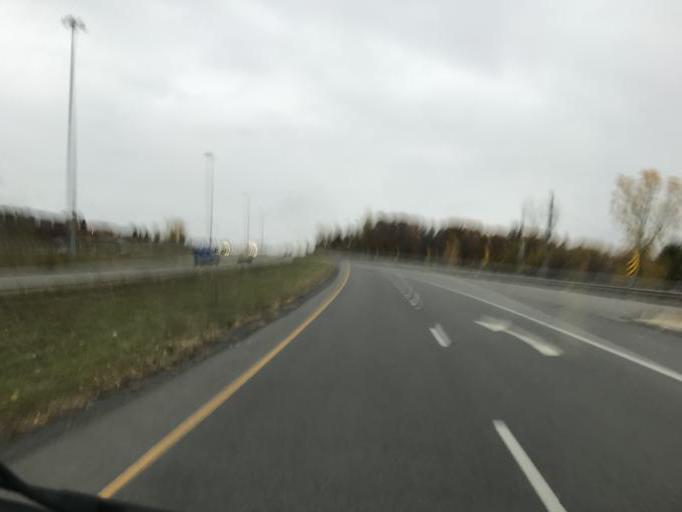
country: CA
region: Quebec
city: Bois-des-Filion
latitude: 45.6758
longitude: -73.7613
